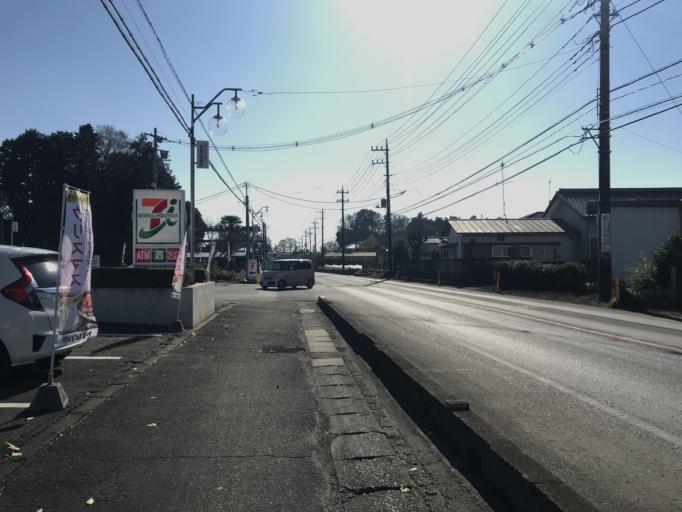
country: JP
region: Ibaraki
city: Sakai
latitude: 36.1546
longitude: 139.8109
